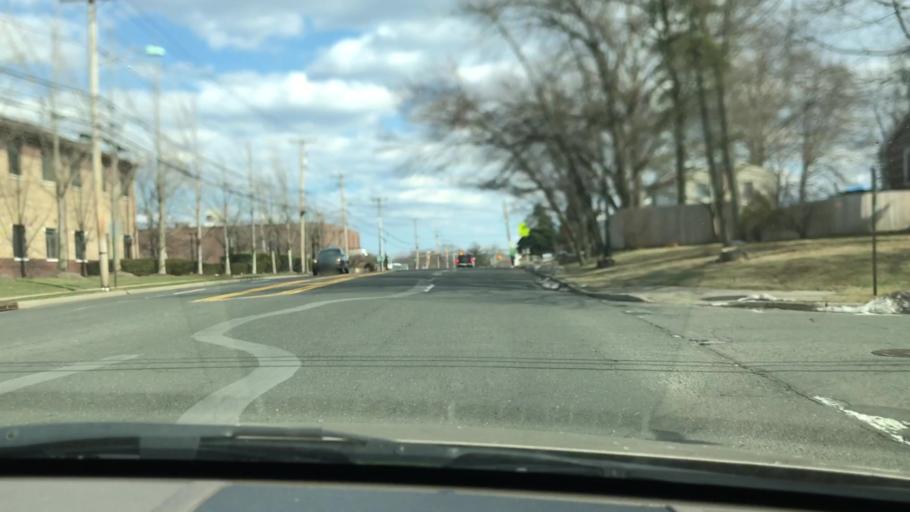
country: US
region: New Jersey
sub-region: Bergen County
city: River Vale
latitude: 40.9825
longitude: -74.0093
